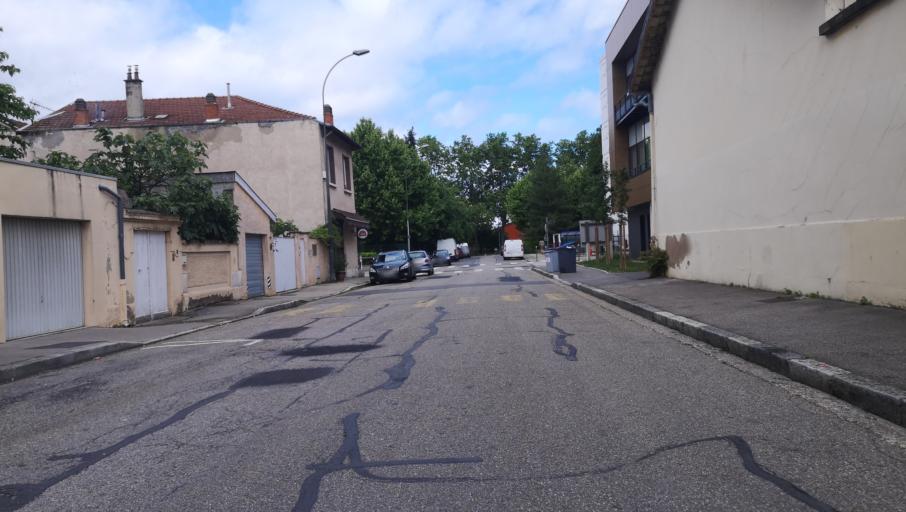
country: FR
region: Rhone-Alpes
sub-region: Departement du Rhone
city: Villeurbanne
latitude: 45.7775
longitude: 4.8698
